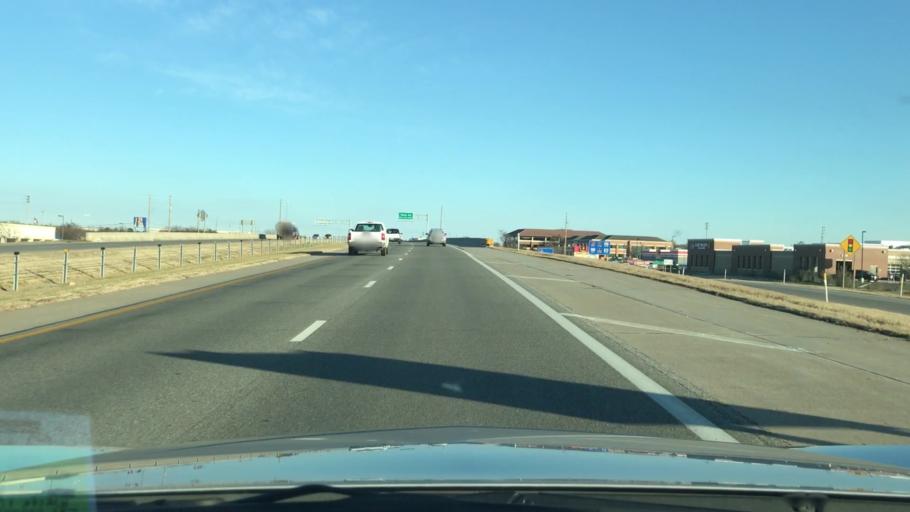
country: US
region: Kansas
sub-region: Sedgwick County
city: Bellaire
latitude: 37.7441
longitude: -97.2474
